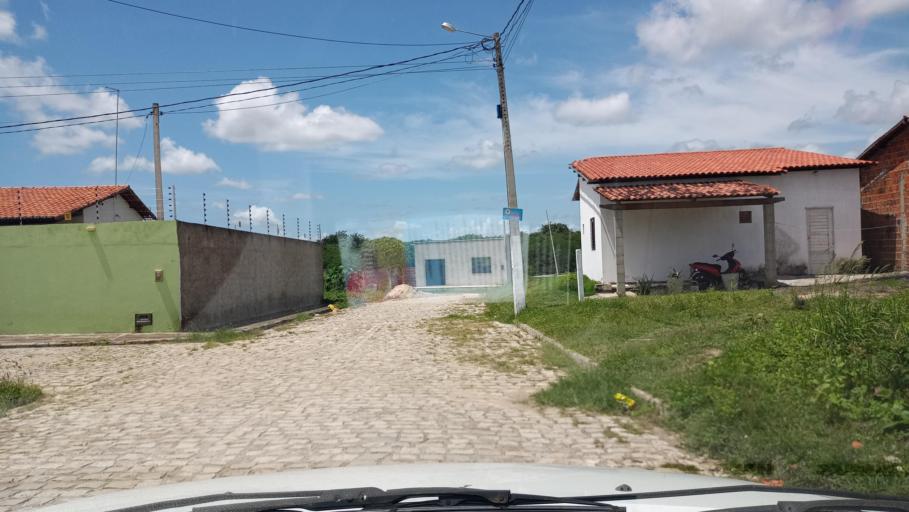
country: BR
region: Rio Grande do Norte
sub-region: Goianinha
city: Goianinha
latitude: -6.2566
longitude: -35.2055
